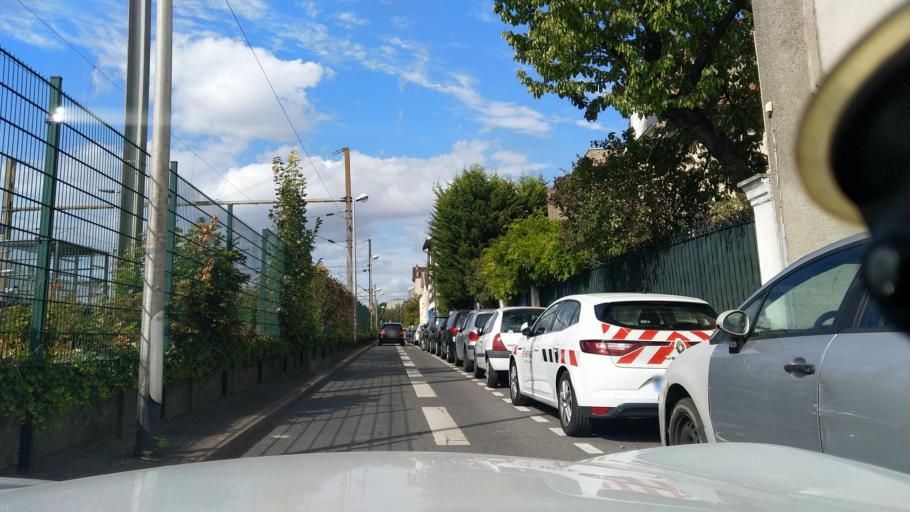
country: FR
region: Ile-de-France
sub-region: Departement du Val-de-Marne
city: Le Perreux-sur-Marne
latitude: 48.8396
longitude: 2.4944
